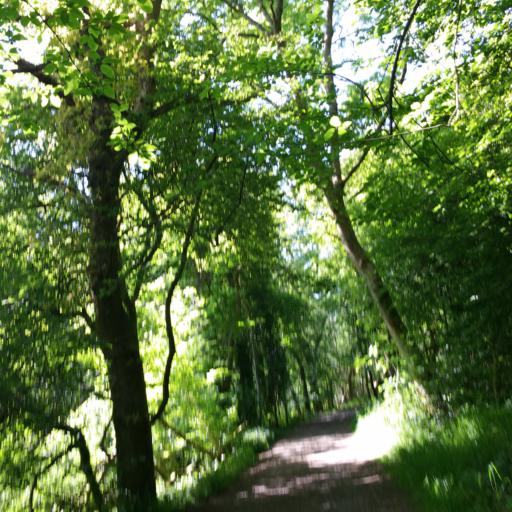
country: GB
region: Scotland
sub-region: East Dunbartonshire
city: Milngavie
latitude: 55.9592
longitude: -4.3325
